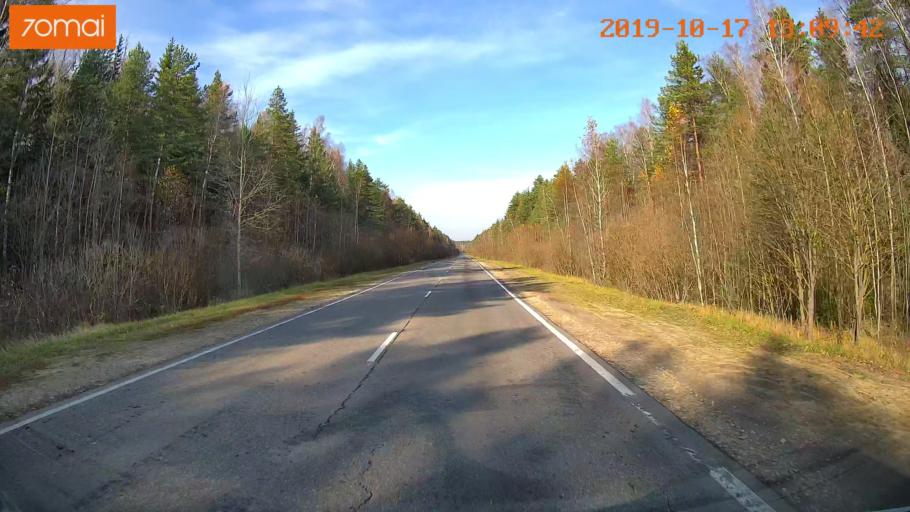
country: RU
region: Rjazan
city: Syntul
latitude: 55.0078
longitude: 41.2613
